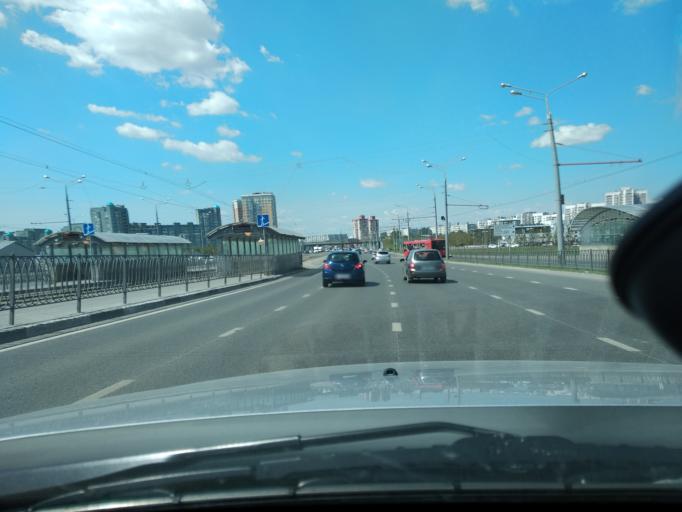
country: RU
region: Tatarstan
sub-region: Gorod Kazan'
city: Kazan
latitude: 55.8232
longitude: 49.1644
